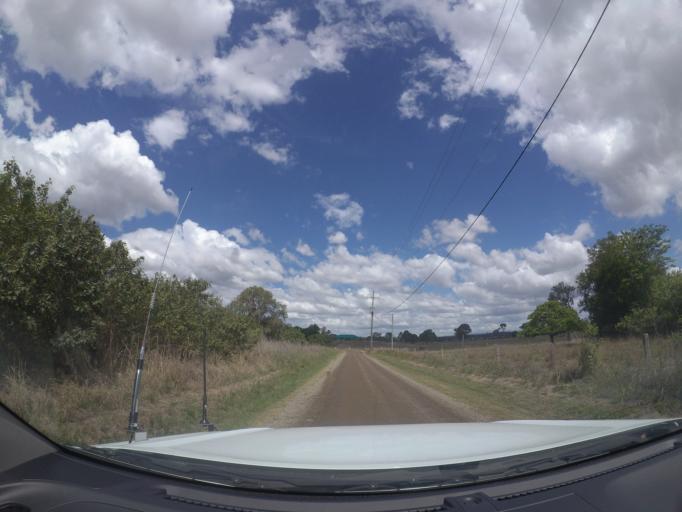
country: AU
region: Queensland
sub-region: Logan
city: Cedar Vale
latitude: -27.9069
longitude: 152.9761
